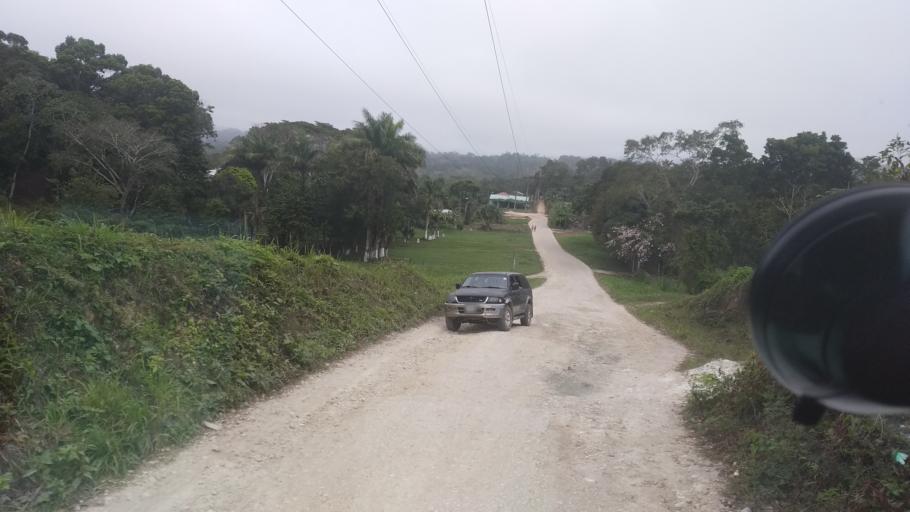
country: BZ
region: Cayo
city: Benque Viejo del Carmen
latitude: 17.0810
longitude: -89.1246
